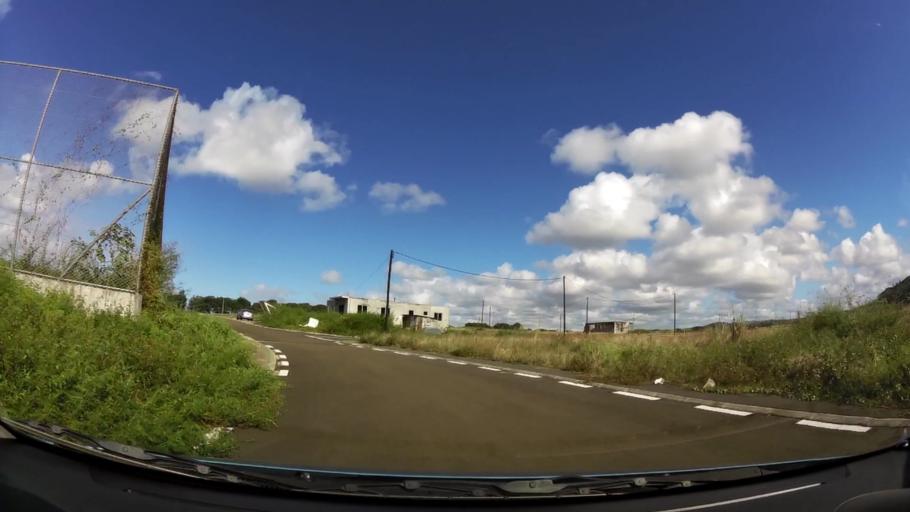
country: MU
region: Grand Port
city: Mahebourg
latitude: -20.4048
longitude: 57.6915
